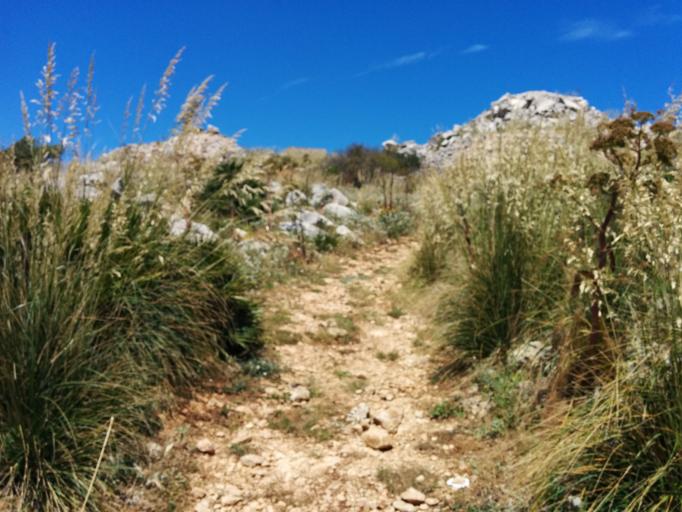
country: IT
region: Sicily
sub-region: Trapani
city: San Vito Lo Capo
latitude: 38.1658
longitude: 12.7579
